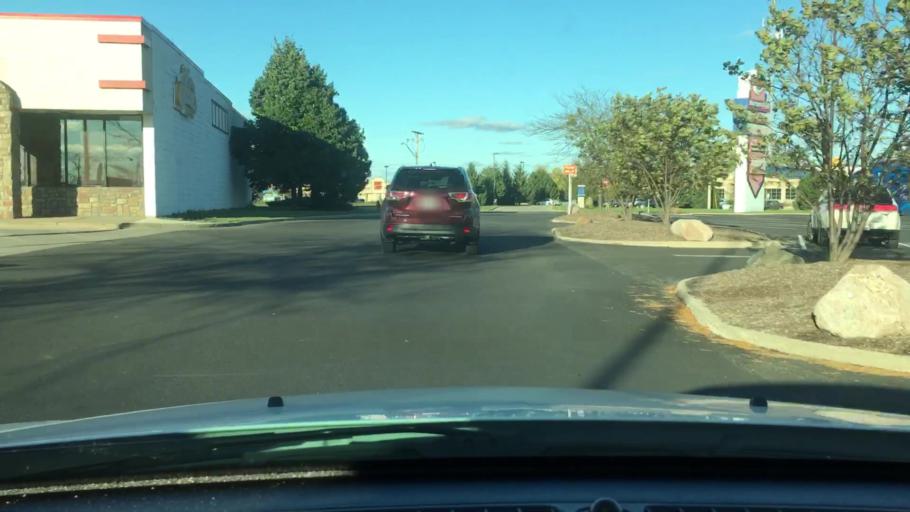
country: US
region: Illinois
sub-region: DeKalb County
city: DeKalb
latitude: 41.9509
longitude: -88.7234
